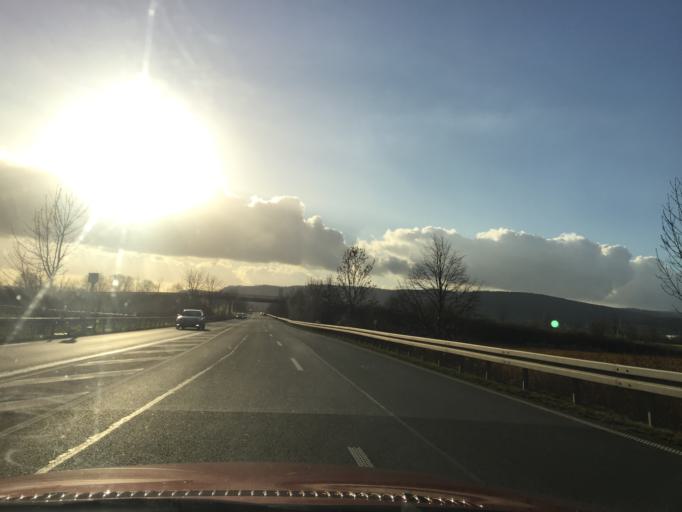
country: DE
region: Lower Saxony
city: Holzminden
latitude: 51.8300
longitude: 9.4318
